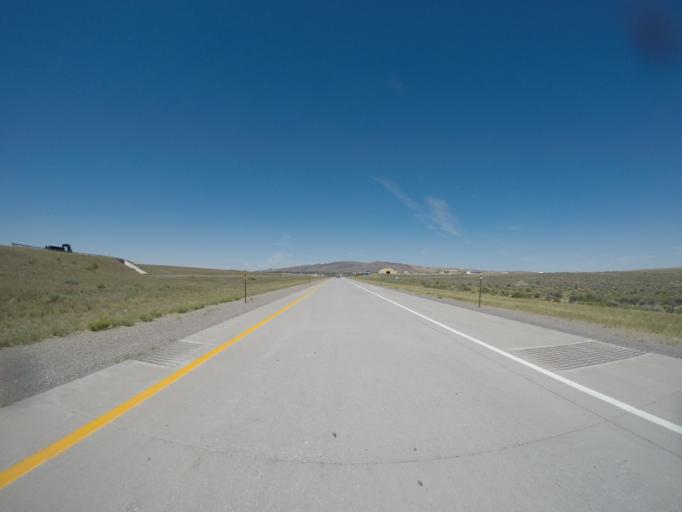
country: US
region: Wyoming
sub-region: Carbon County
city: Rawlins
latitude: 41.7900
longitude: -107.1986
